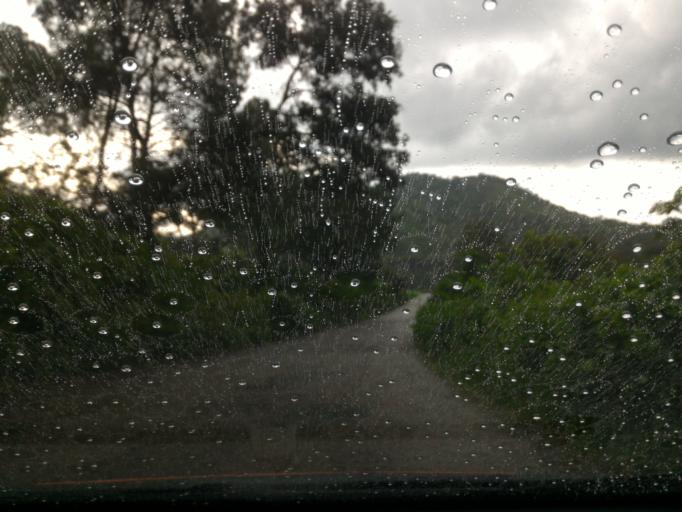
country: MX
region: Jalisco
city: San Andres Ixtlan
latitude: 19.8485
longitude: -103.4597
